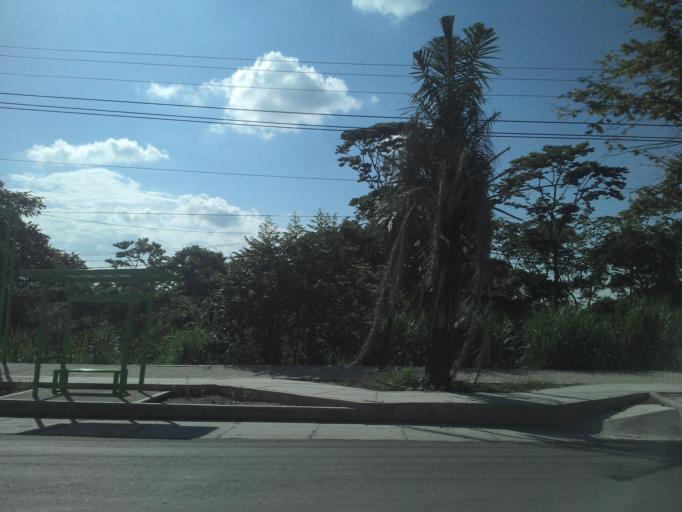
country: MX
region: Chiapas
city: Palenque
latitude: 17.5204
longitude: -91.9933
